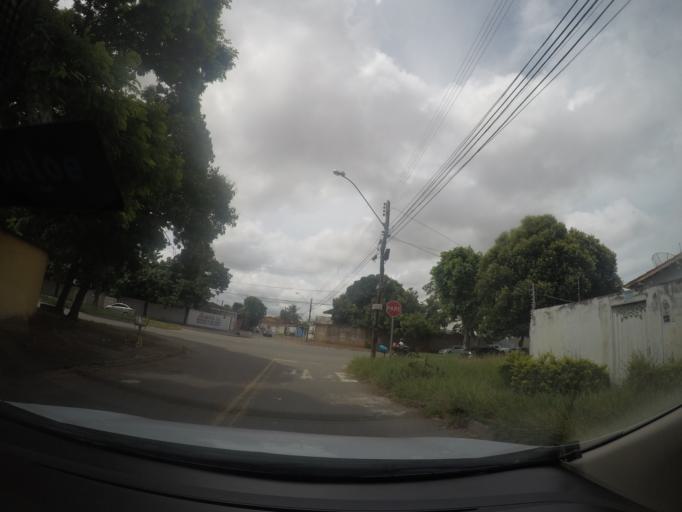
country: BR
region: Goias
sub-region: Goiania
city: Goiania
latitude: -16.7156
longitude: -49.3062
